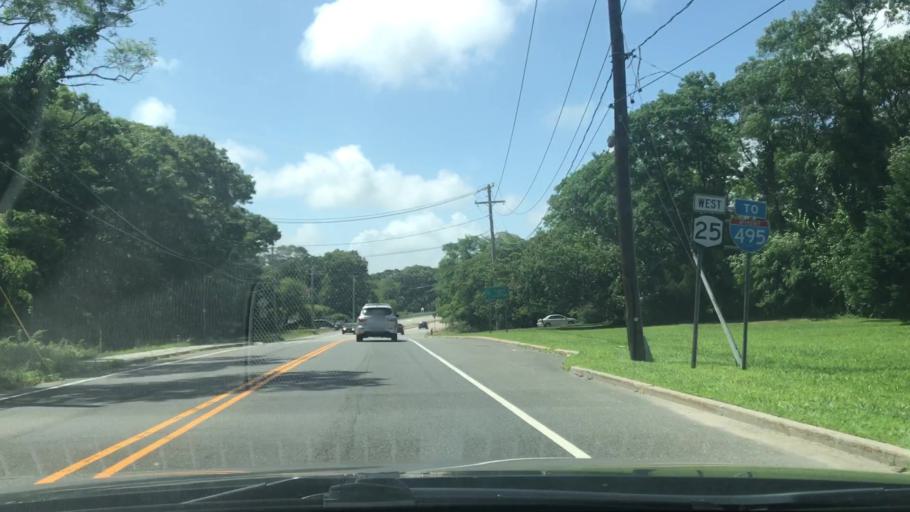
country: US
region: New York
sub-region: Suffolk County
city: Calverton
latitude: 40.9176
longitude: -72.7176
